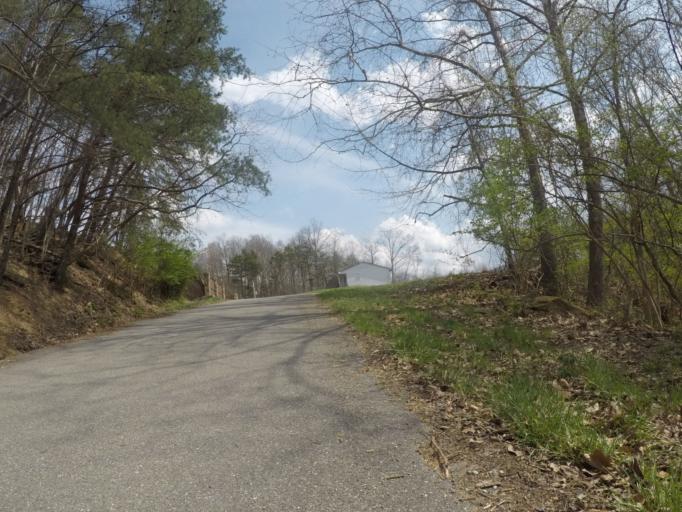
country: US
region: West Virginia
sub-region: Cabell County
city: Pea Ridge
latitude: 38.3989
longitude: -82.3364
